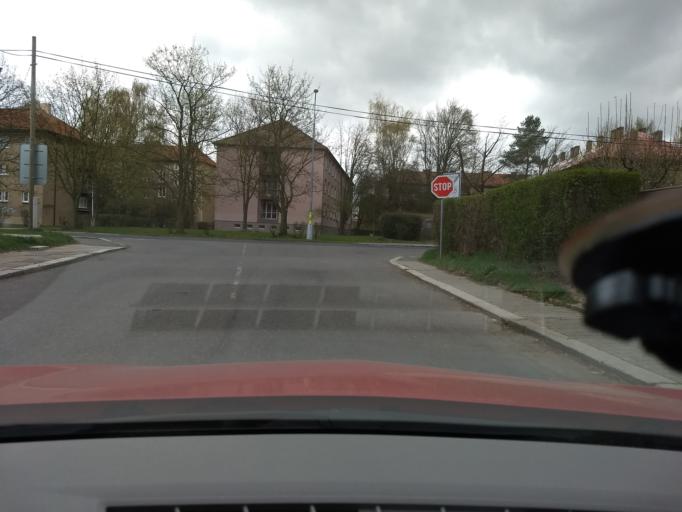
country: CZ
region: Central Bohemia
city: Kladno
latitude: 50.1355
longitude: 14.1220
